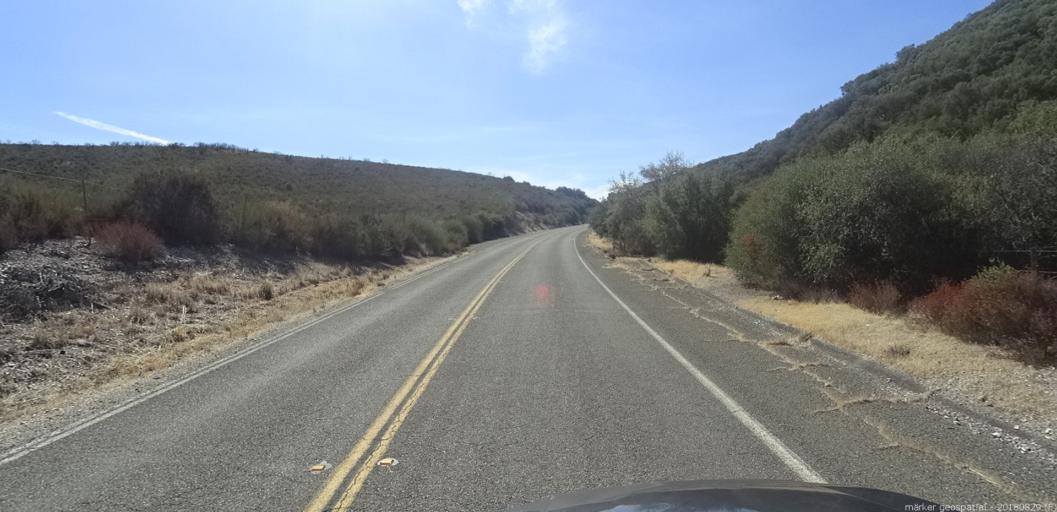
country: US
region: California
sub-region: San Luis Obispo County
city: Lake Nacimiento
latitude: 35.8546
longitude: -121.0562
